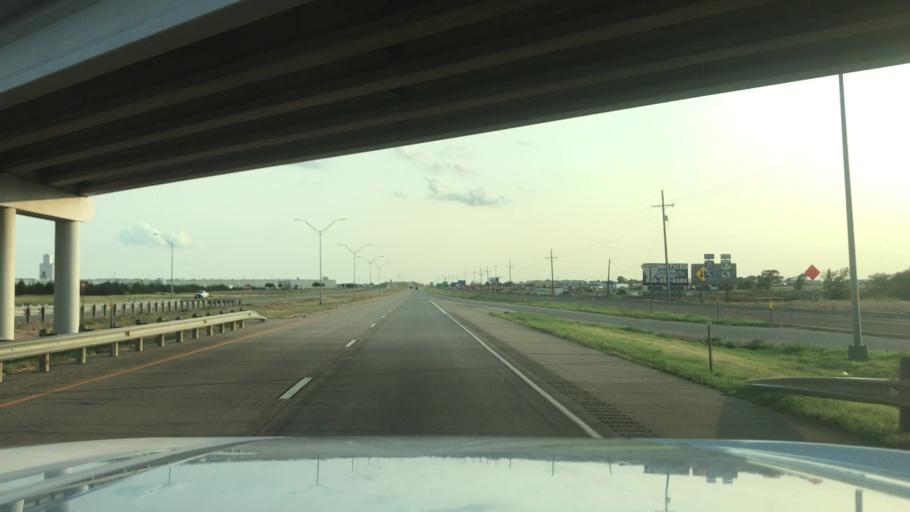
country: US
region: Texas
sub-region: Hale County
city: Seth Ward
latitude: 34.2193
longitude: -101.7256
